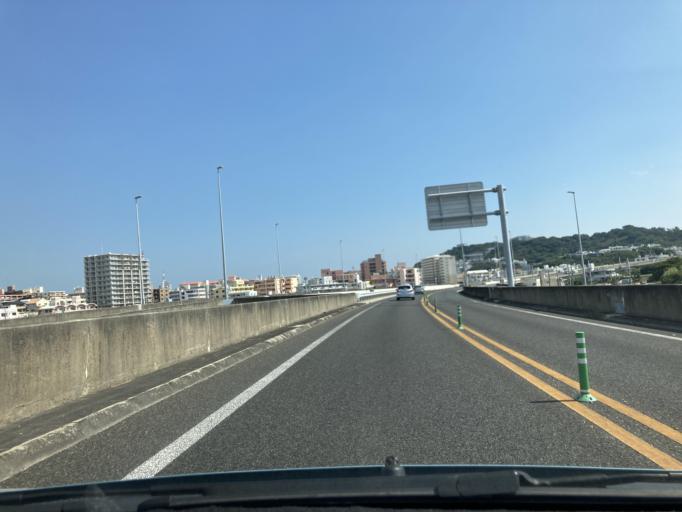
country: JP
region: Okinawa
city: Tomigusuku
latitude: 26.1759
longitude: 127.6708
